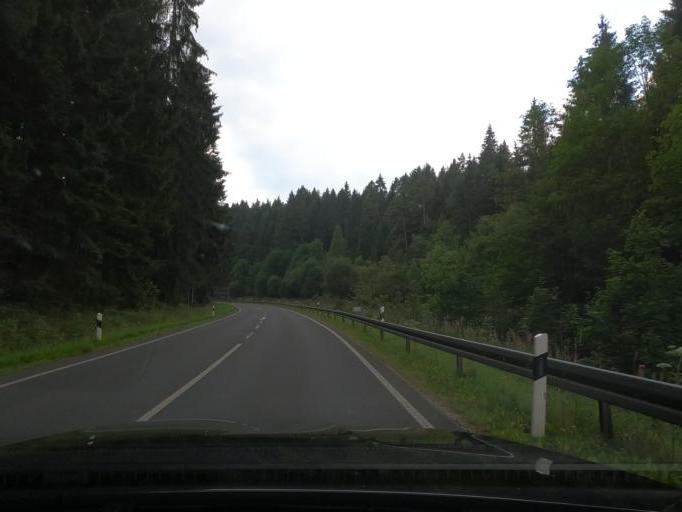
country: DE
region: Lower Saxony
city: Wildemann
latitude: 51.8116
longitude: 10.2809
